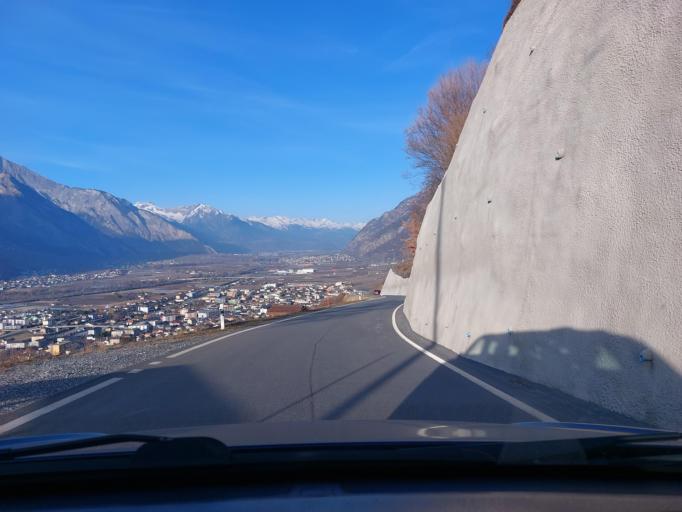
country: CH
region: Valais
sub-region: Martigny District
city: Saxon
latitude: 46.1421
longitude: 7.1710
